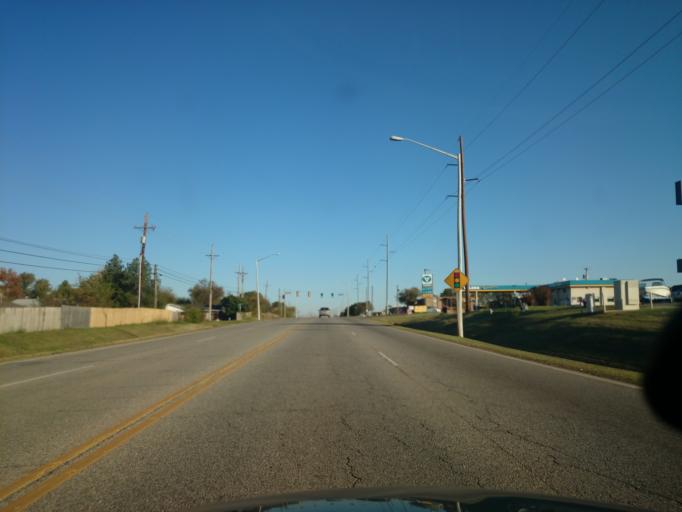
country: US
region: Oklahoma
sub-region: Payne County
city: Stillwater
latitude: 36.1472
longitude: -97.0516
